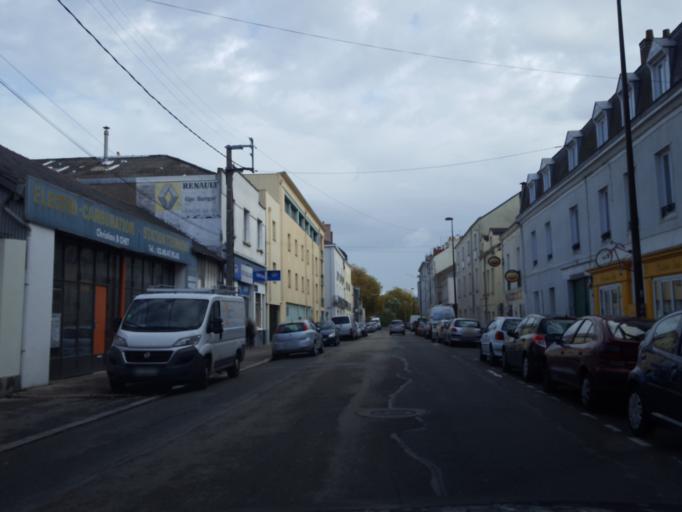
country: FR
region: Pays de la Loire
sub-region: Departement de la Loire-Atlantique
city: Nantes
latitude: 47.2066
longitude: -1.5545
